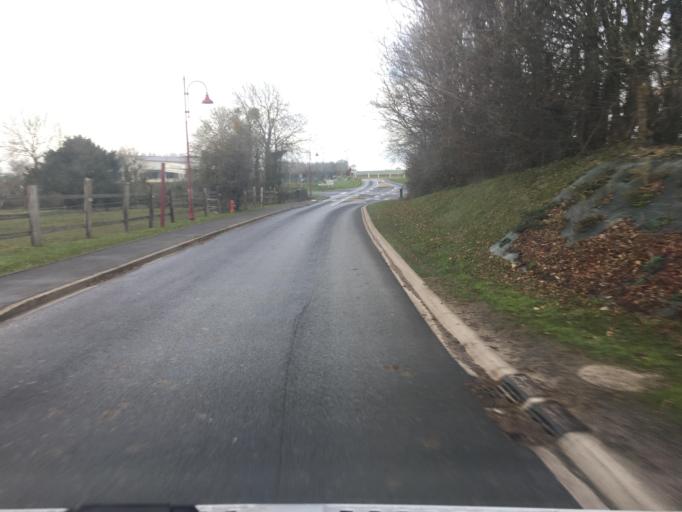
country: FR
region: Lower Normandy
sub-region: Departement du Calvados
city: Creully
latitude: 49.2530
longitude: -0.5631
